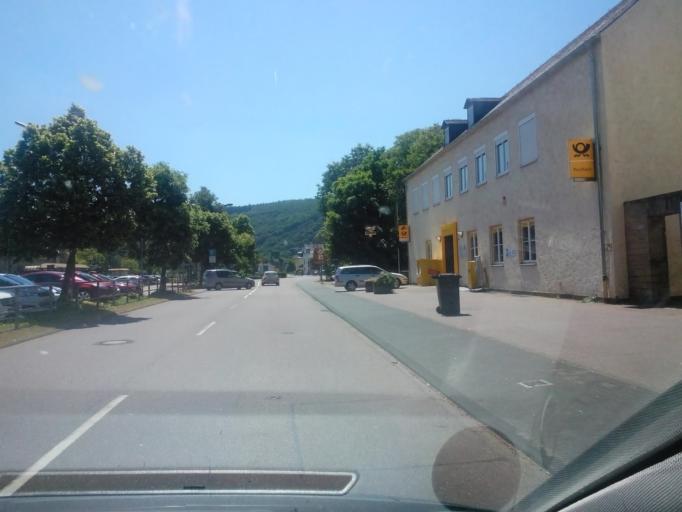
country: DE
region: Rheinland-Pfalz
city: Saarburg
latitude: 49.6074
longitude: 6.5571
